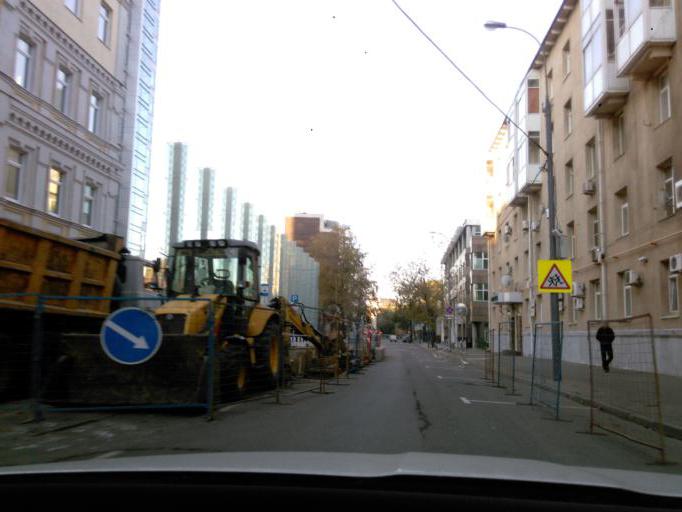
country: RU
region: Moscow
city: Moscow
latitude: 55.7692
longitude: 37.5904
